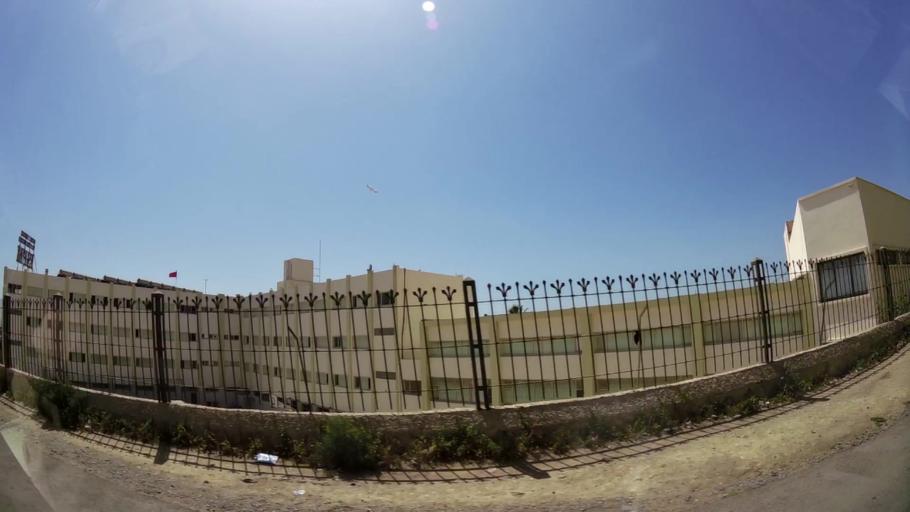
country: MA
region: Souss-Massa-Draa
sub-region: Agadir-Ida-ou-Tnan
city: Agadir
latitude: 30.4285
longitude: -9.6338
